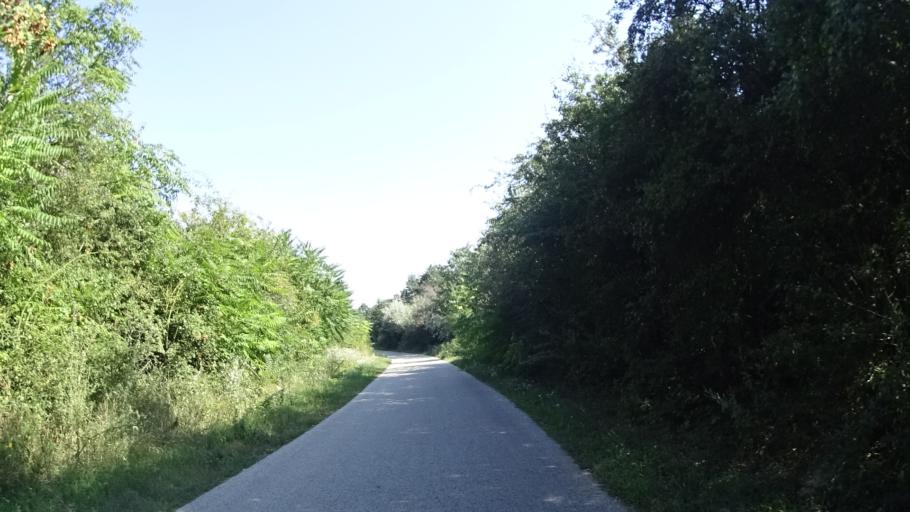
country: HU
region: Fejer
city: Pakozd
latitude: 47.2228
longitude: 18.5816
